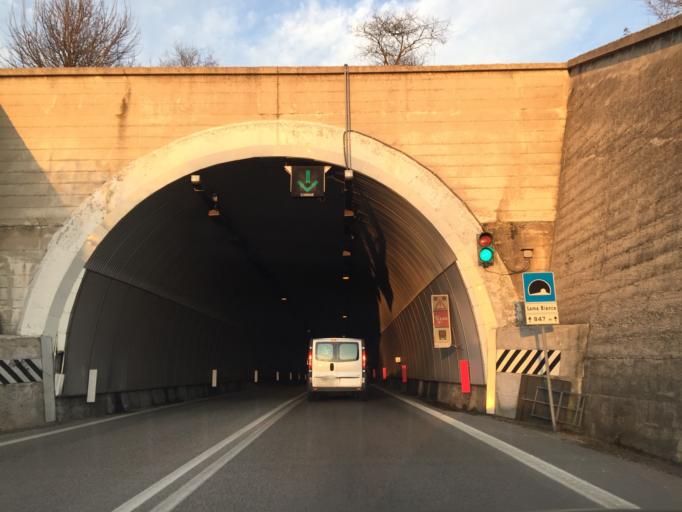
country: IT
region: Molise
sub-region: Provincia di Campobasso
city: Mimosa-Poggio Verde-Nuova Comunita
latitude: 41.5455
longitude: 14.6273
